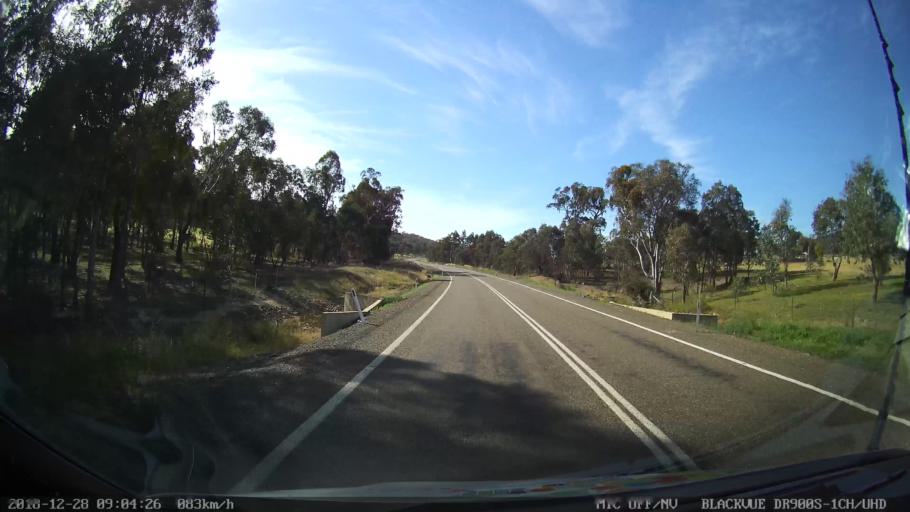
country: AU
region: New South Wales
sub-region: Upper Lachlan Shire
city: Crookwell
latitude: -34.1730
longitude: 149.3440
